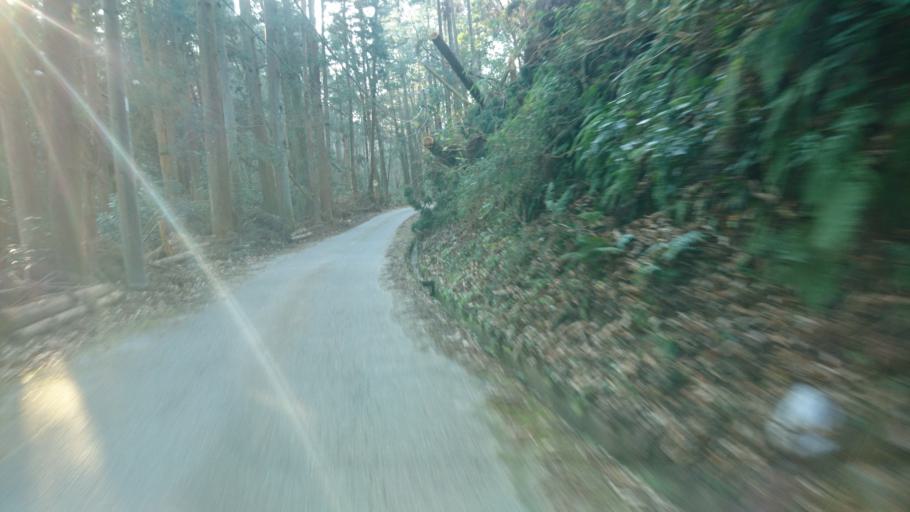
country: JP
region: Chiba
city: Kimitsu
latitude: 35.2895
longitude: 139.9546
